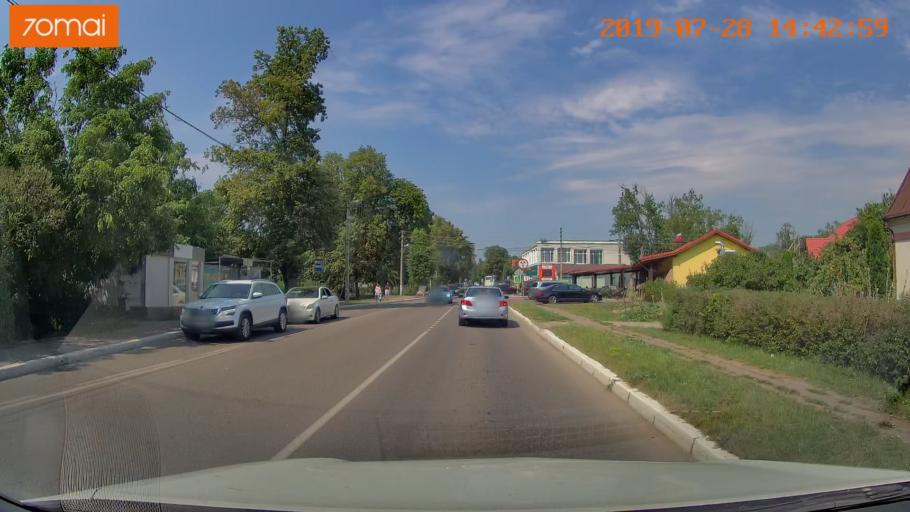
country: RU
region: Kaliningrad
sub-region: Gorod Kaliningrad
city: Yantarnyy
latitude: 54.8629
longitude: 19.9400
